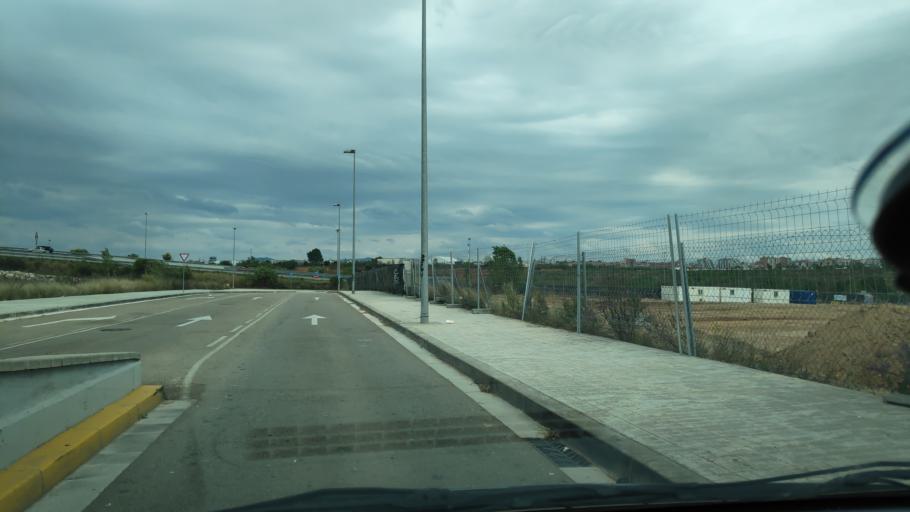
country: ES
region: Catalonia
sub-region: Provincia de Barcelona
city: Barbera del Valles
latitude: 41.5135
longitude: 2.1047
